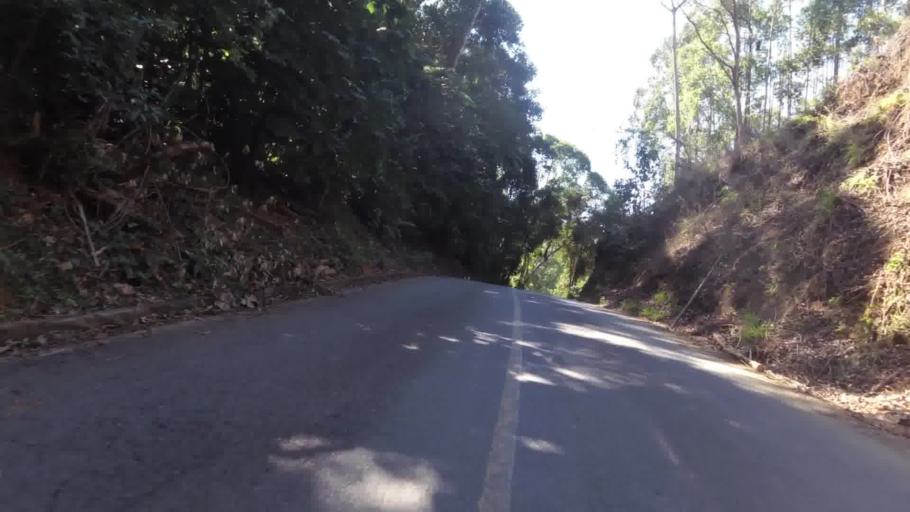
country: BR
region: Espirito Santo
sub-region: Marechal Floriano
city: Marechal Floriano
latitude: -20.4588
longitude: -40.9051
